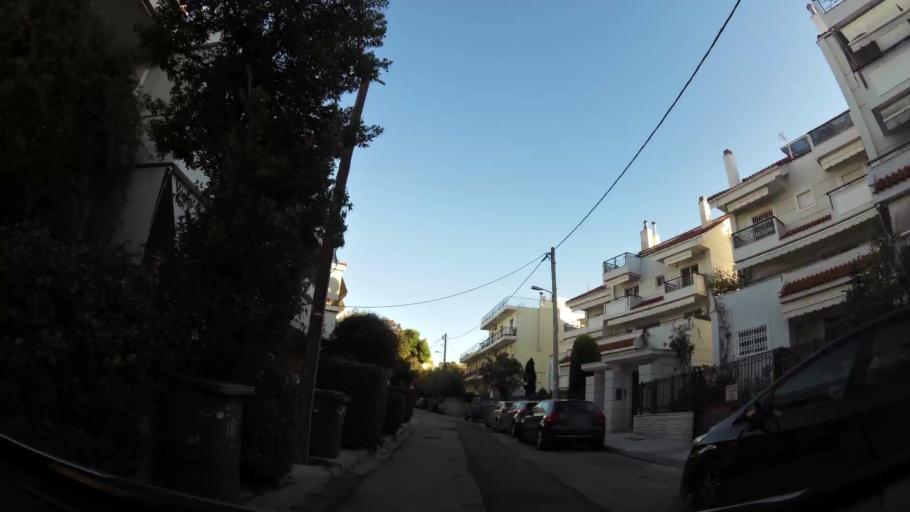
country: GR
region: Attica
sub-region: Nomarchia Athinas
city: Kifisia
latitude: 38.0706
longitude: 23.8008
